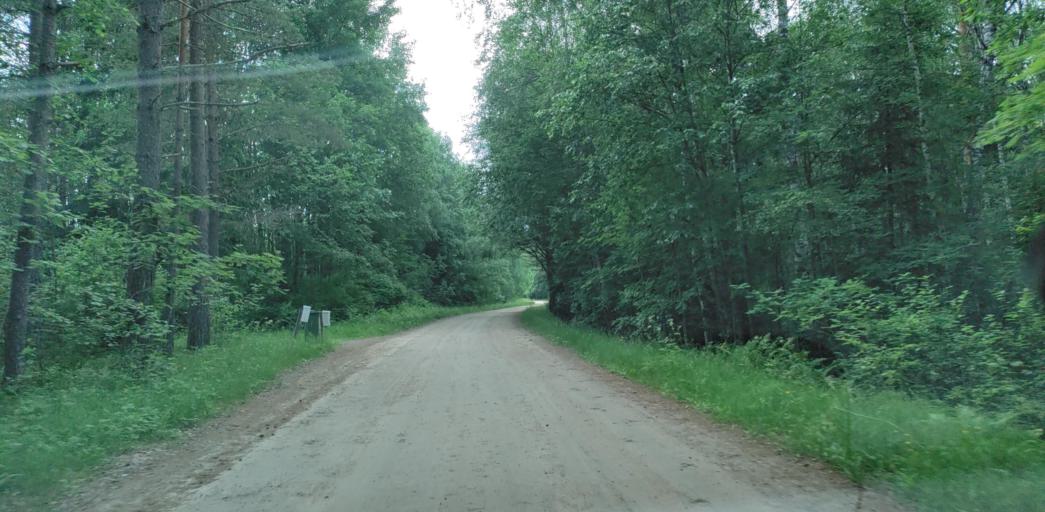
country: SE
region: Vaermland
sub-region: Hagfors Kommun
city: Hagfors
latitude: 60.0605
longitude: 13.5752
